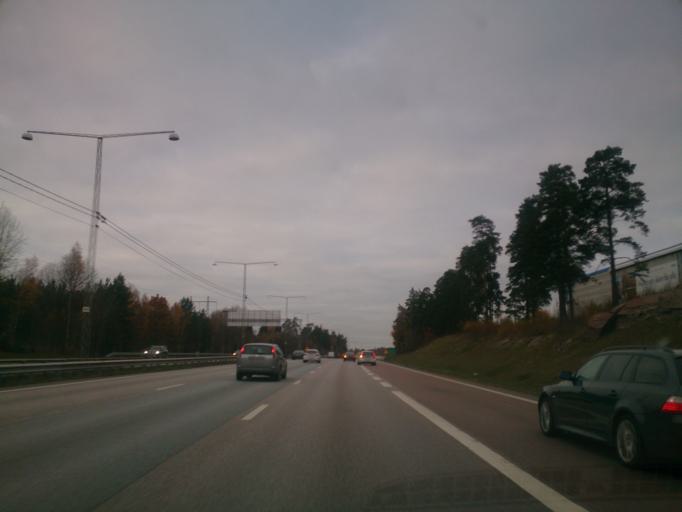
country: SE
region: Stockholm
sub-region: Sollentuna Kommun
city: Sollentuna
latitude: 59.4431
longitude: 17.9223
